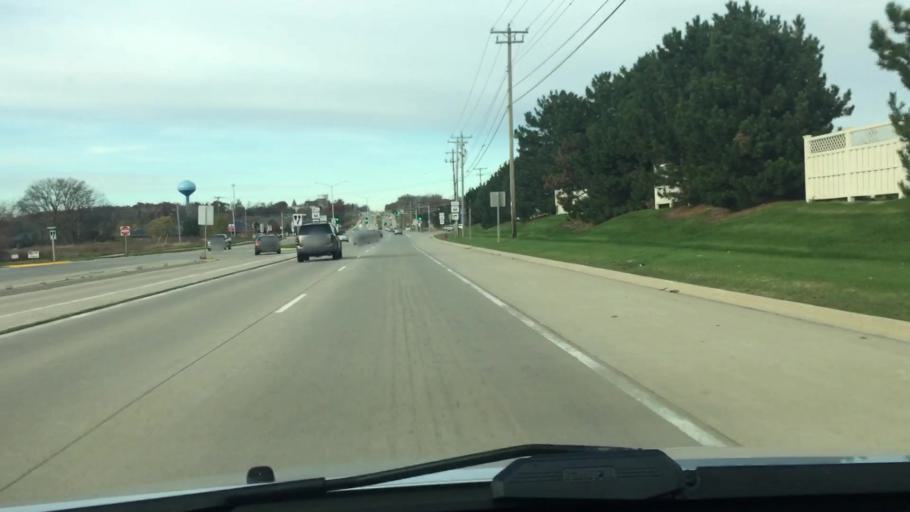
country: US
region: Wisconsin
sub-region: Waukesha County
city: Pewaukee
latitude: 43.0664
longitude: -88.2250
